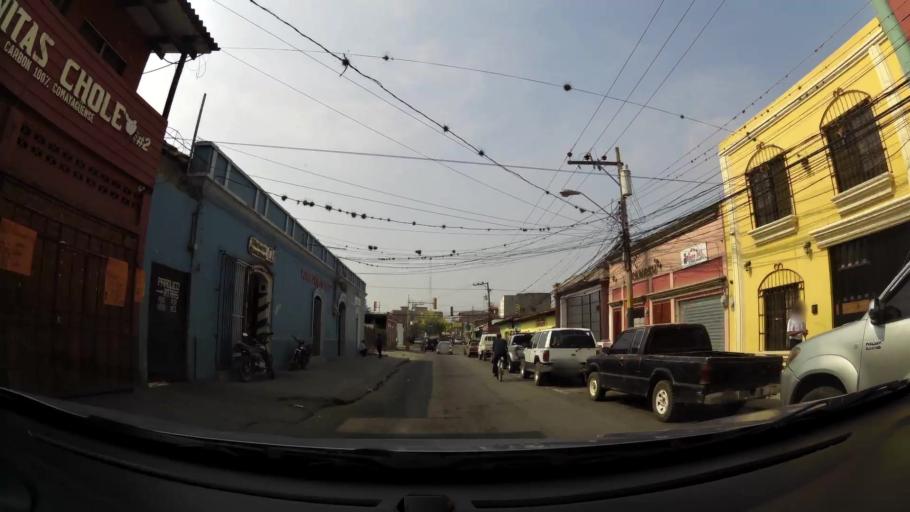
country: HN
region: Comayagua
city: Comayagua
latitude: 14.4568
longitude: -87.6398
